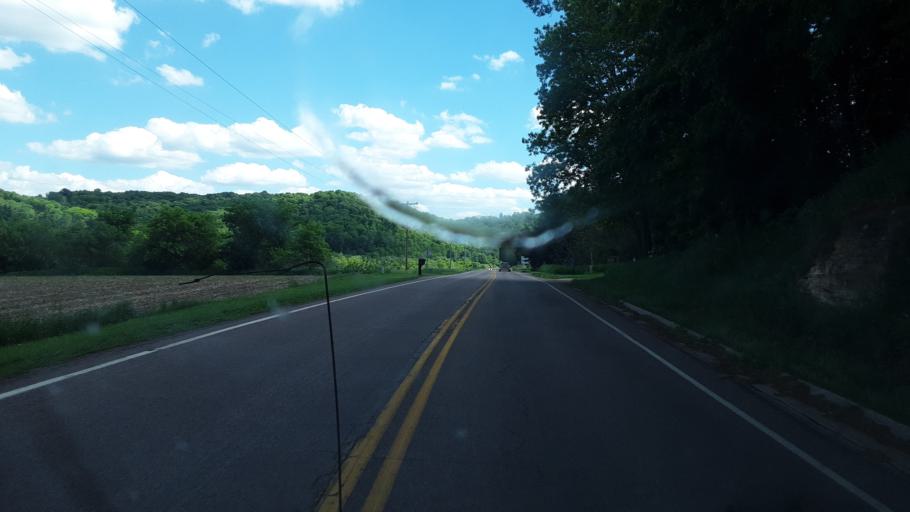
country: US
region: Wisconsin
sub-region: Richland County
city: Richland Center
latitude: 43.4017
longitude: -90.2434
